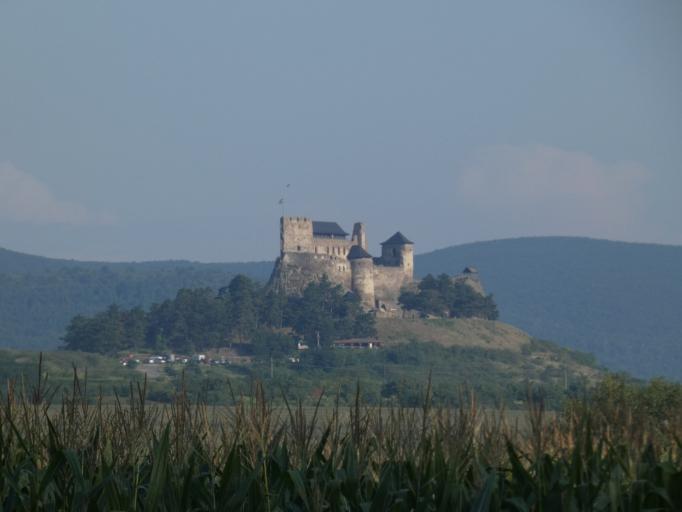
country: HU
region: Borsod-Abauj-Zemplen
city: Abaujszanto
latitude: 48.3612
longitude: 21.2155
